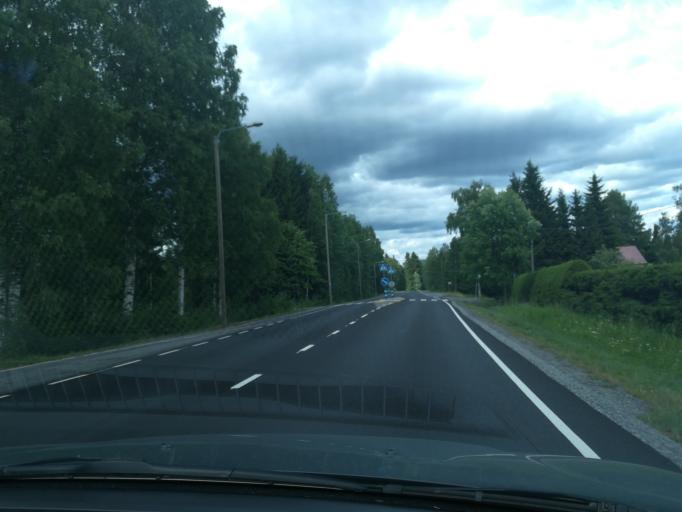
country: FI
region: Southern Savonia
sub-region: Mikkeli
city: Mikkeli
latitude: 61.6463
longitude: 27.0819
